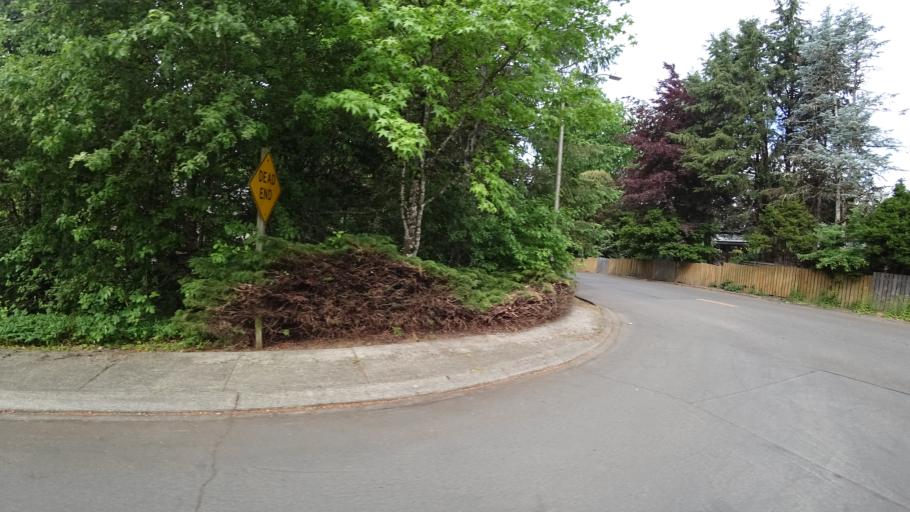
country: US
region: Oregon
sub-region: Clackamas County
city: Lake Oswego
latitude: 45.4301
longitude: -122.6839
